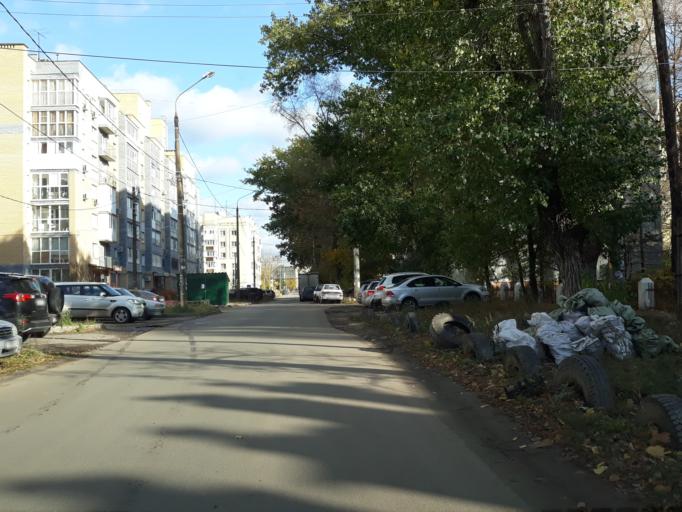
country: RU
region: Nizjnij Novgorod
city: Nizhniy Novgorod
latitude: 56.3030
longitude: 43.9357
